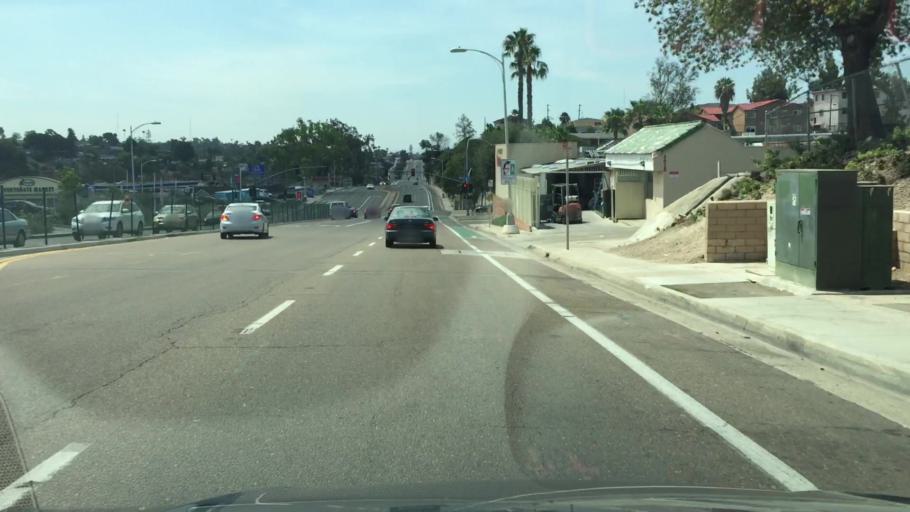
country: US
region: California
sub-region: San Diego County
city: Lemon Grove
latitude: 32.7501
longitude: -117.0796
